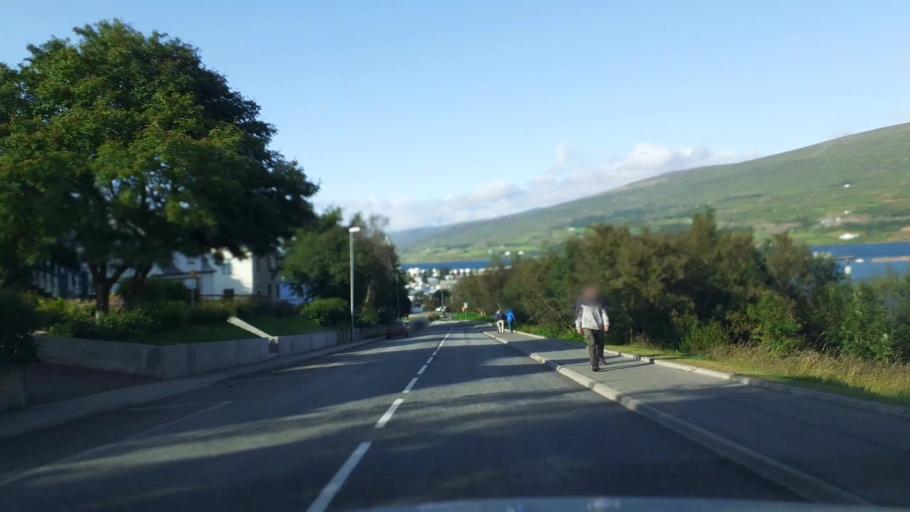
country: IS
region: Northeast
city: Akureyri
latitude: 65.6781
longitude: -18.0917
